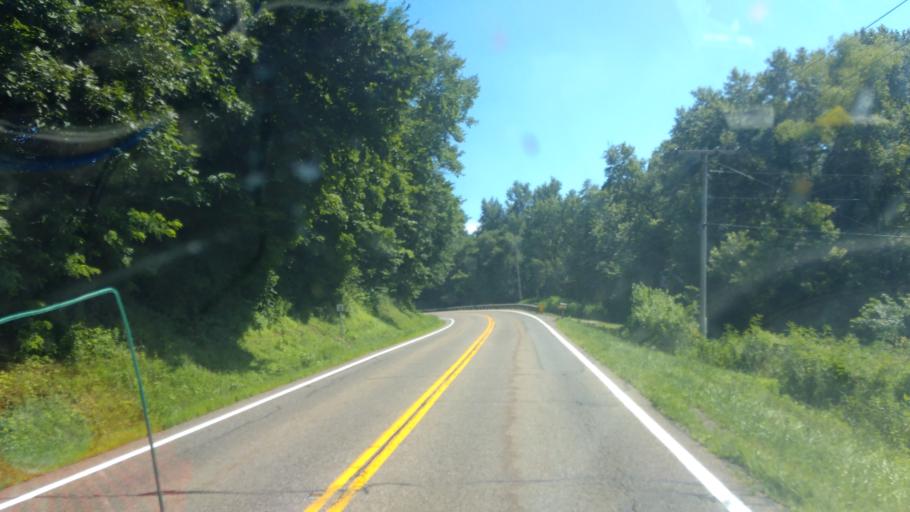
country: US
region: Ohio
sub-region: Carroll County
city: Carrollton
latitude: 40.5589
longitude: -81.1551
